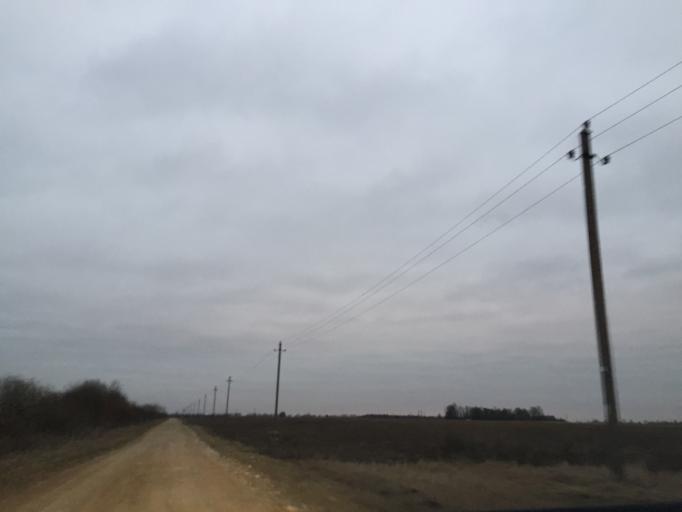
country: LT
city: Zagare
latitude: 56.3401
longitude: 23.2675
